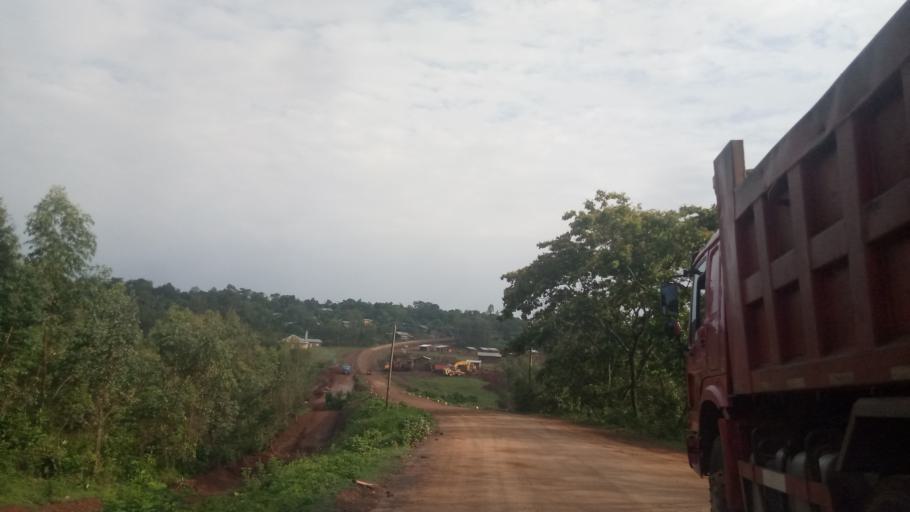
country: ET
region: Oromiya
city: Agaro
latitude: 7.8552
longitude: 36.6540
